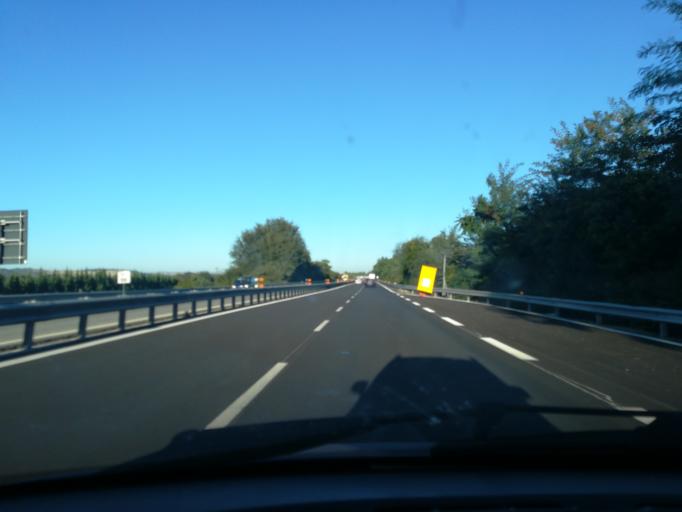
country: IT
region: The Marches
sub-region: Provincia di Macerata
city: Zona Industriale
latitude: 43.2569
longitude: 13.4564
